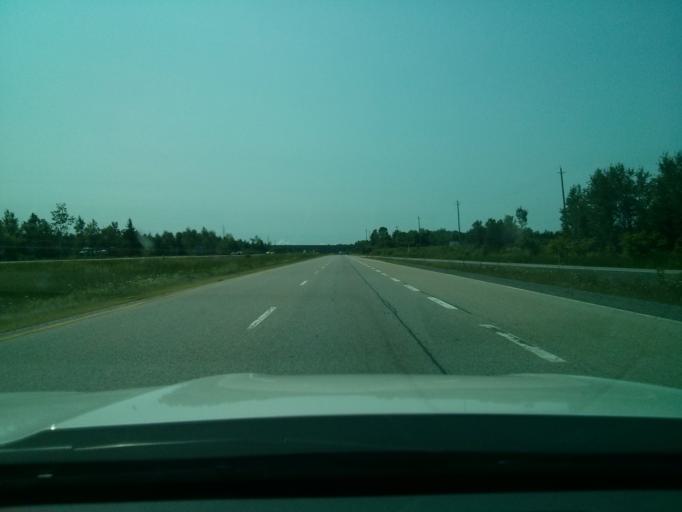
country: CA
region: Ontario
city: Prescott
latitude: 45.0272
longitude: -75.6267
